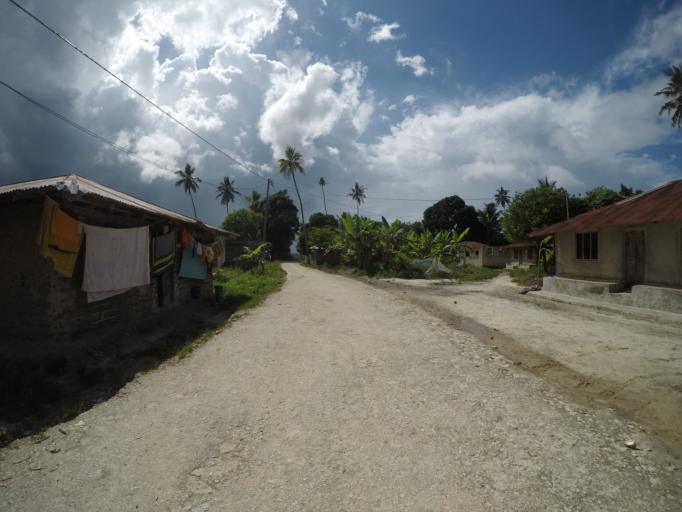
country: TZ
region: Pemba South
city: Mtambile
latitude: -5.3504
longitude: 39.7016
